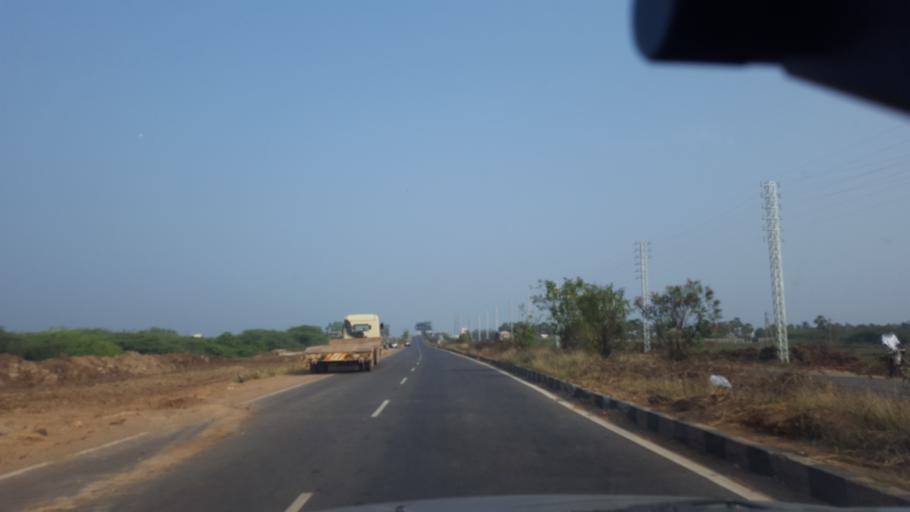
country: IN
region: Andhra Pradesh
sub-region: West Godavari
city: Eluru
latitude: 16.7394
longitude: 81.1069
